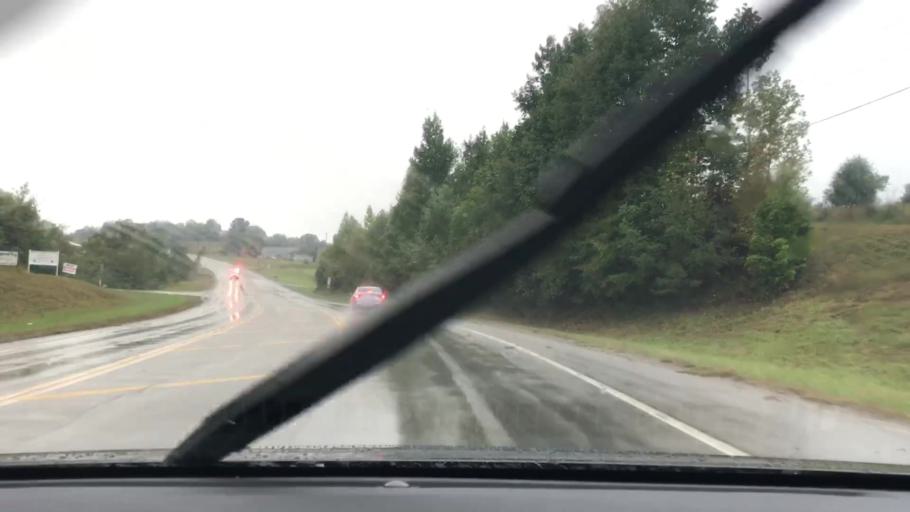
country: US
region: Tennessee
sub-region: Sumner County
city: Westmoreland
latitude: 36.5237
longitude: -86.1746
